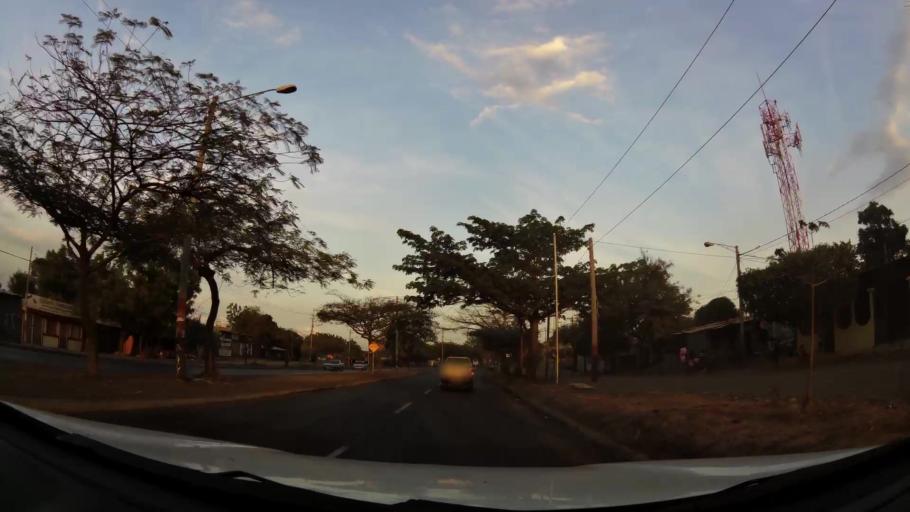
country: NI
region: Managua
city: Managua
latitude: 12.1416
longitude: -86.2180
